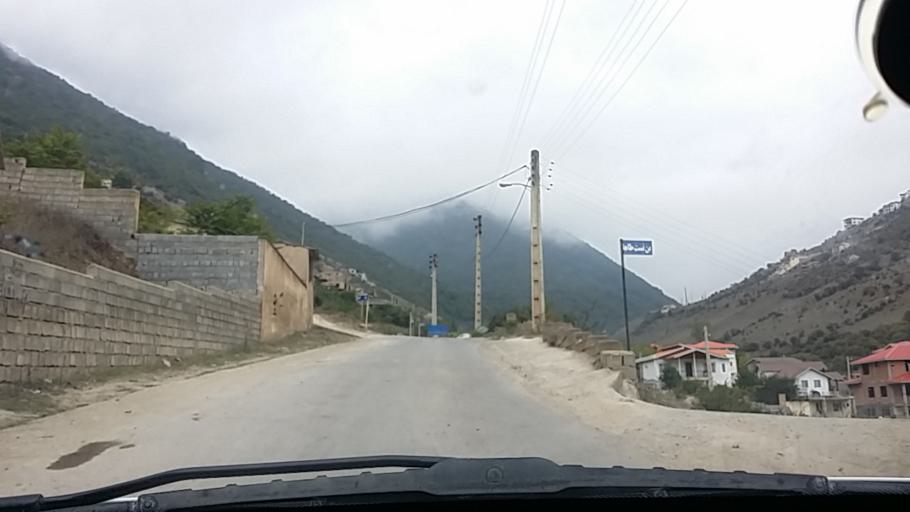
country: IR
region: Mazandaran
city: `Abbasabad
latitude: 36.4753
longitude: 51.1401
